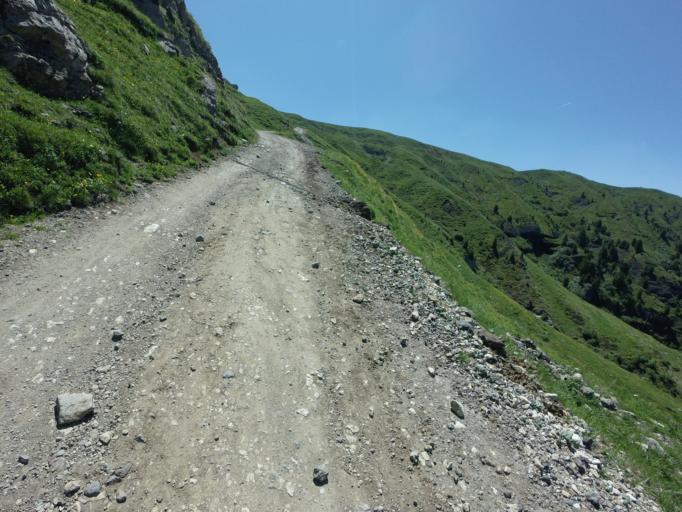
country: IT
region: Trentino-Alto Adige
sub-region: Provincia di Trento
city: Mazzin
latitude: 46.5079
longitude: 11.6969
